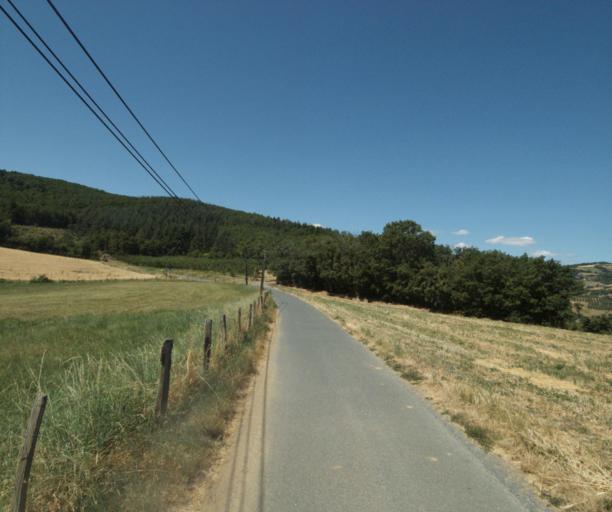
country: FR
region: Rhone-Alpes
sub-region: Departement du Rhone
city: Bessenay
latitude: 45.7857
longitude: 4.5272
